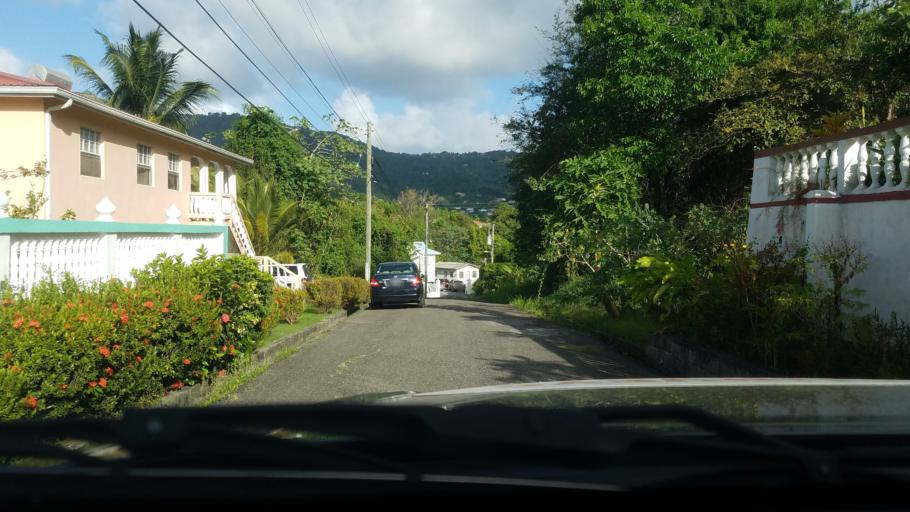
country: LC
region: Castries Quarter
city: Bisee
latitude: 14.0378
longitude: -60.9549
